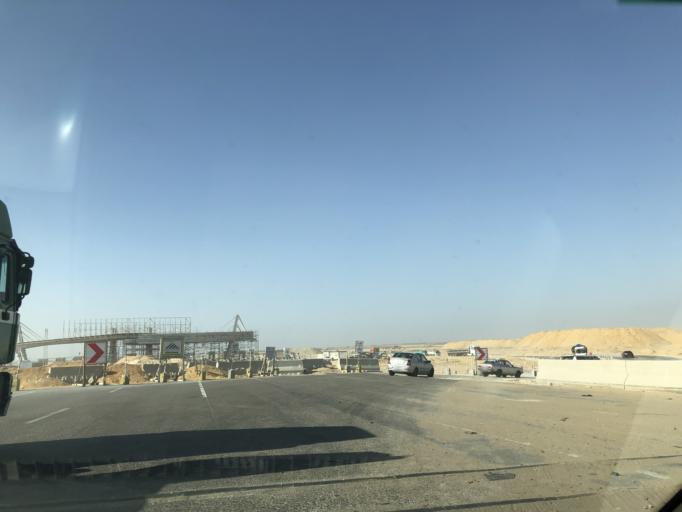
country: EG
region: Muhafazat al Minufiyah
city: Ashmun
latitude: 30.0598
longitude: 30.8460
